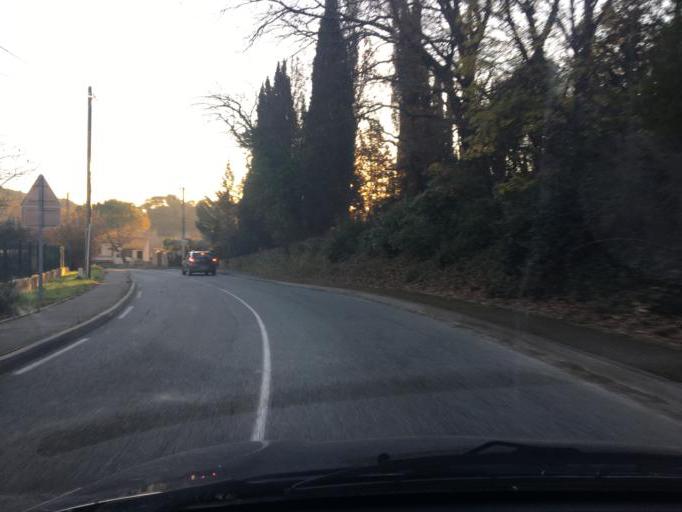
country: FR
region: Provence-Alpes-Cote d'Azur
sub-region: Departement du Var
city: Taradeau
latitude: 43.4530
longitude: 6.4218
